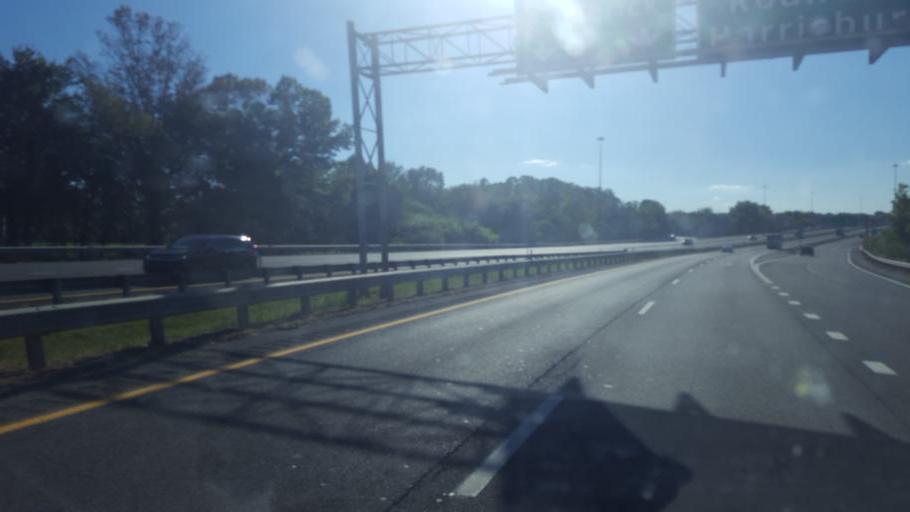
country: US
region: Maryland
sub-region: Washington County
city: Halfway
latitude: 39.6215
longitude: -77.7897
